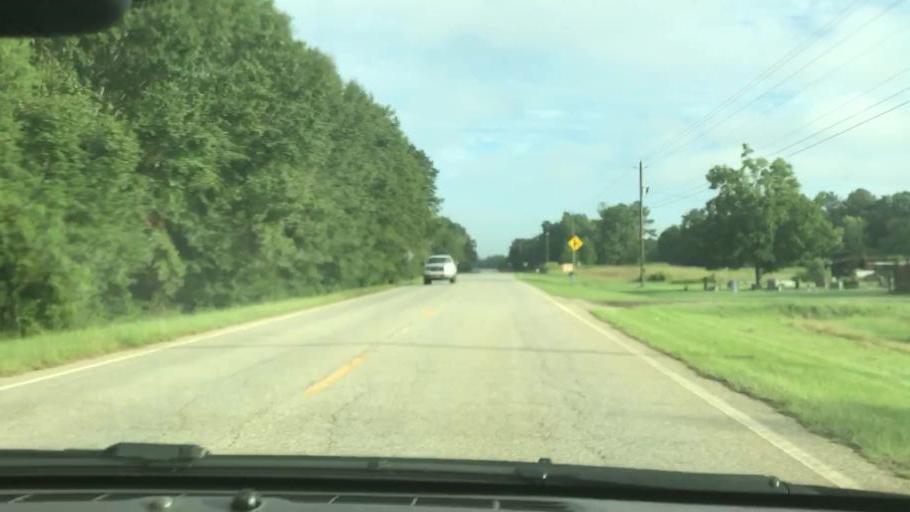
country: US
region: Georgia
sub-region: Clay County
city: Fort Gaines
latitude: 31.7307
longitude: -85.0467
